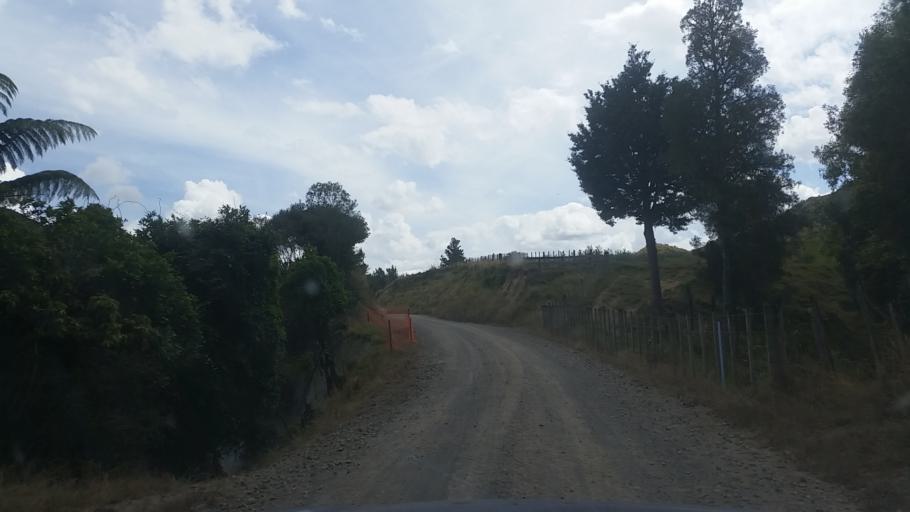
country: NZ
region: Taranaki
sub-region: New Plymouth District
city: Waitara
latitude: -39.1068
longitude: 174.8469
